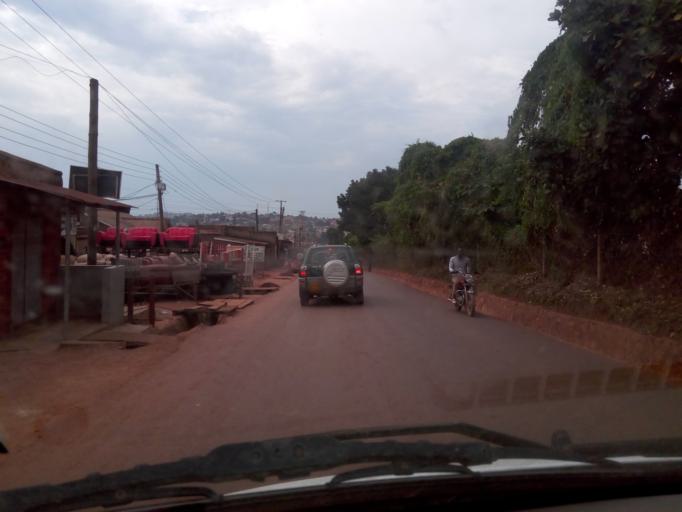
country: UG
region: Central Region
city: Kampala Central Division
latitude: 0.3452
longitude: 32.5772
